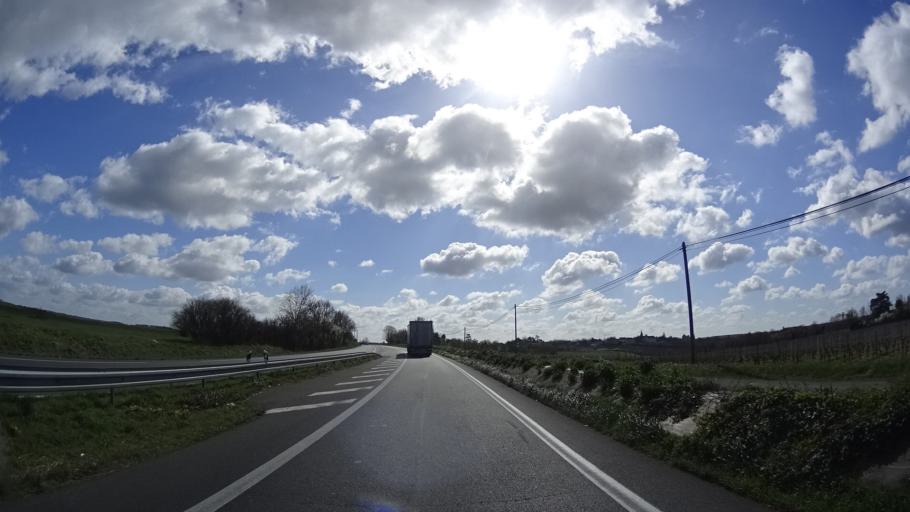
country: FR
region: Pays de la Loire
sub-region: Departement de Maine-et-Loire
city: Brissac-Quince
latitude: 47.3664
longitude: -0.4560
